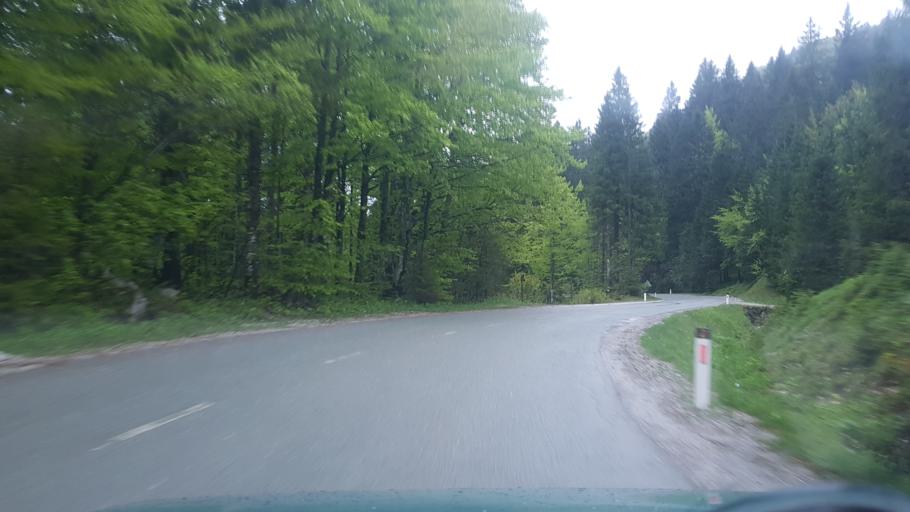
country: SI
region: Bohinj
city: Bohinjska Bistrica
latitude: 46.2406
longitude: 14.0114
